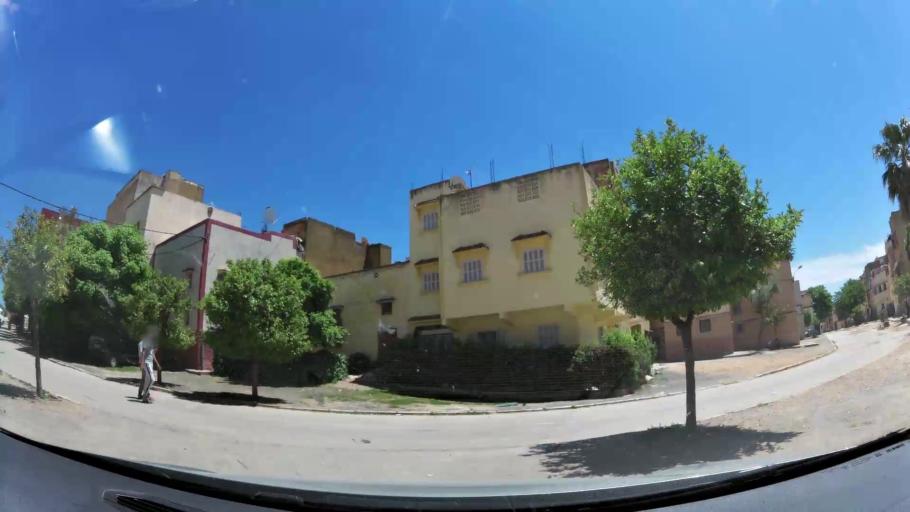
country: MA
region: Meknes-Tafilalet
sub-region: Meknes
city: Meknes
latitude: 33.9125
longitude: -5.5802
